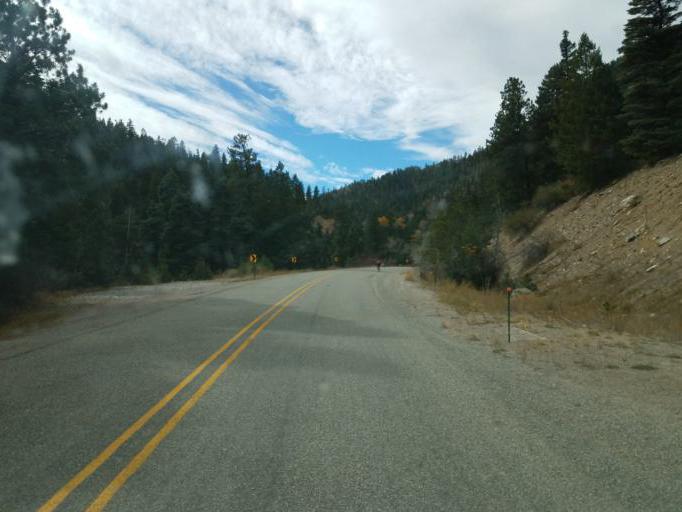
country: US
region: New Mexico
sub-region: Taos County
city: Arroyo Seco
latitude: 36.5616
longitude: -105.5301
